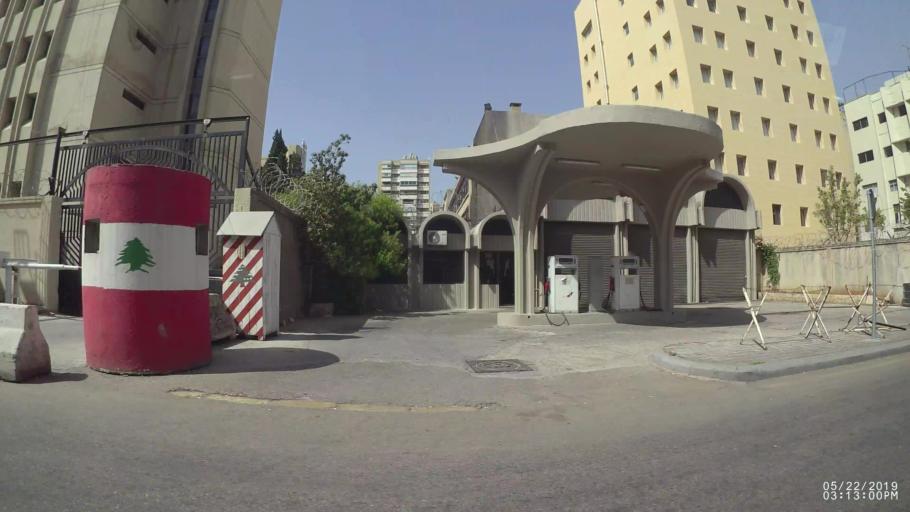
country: LB
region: Beyrouth
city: Beirut
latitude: 33.8807
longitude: 35.4914
